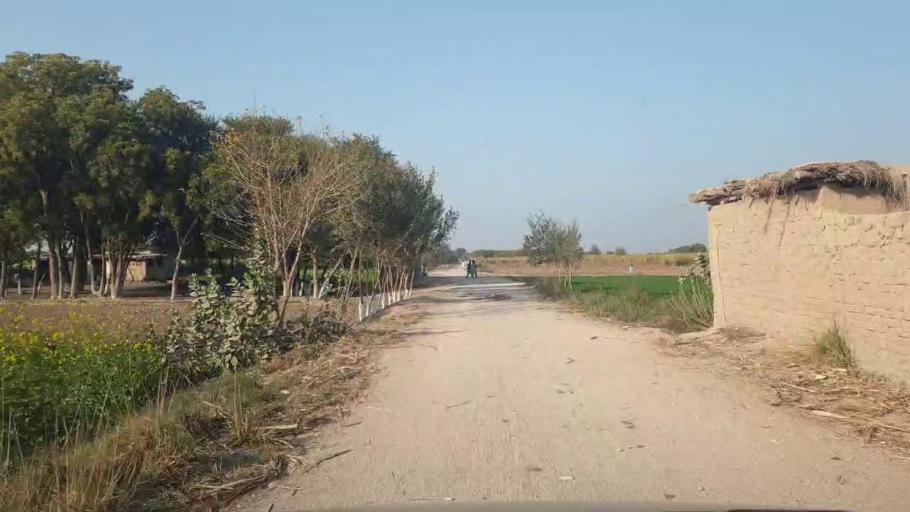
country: PK
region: Sindh
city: Bhit Shah
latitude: 25.8273
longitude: 68.5200
